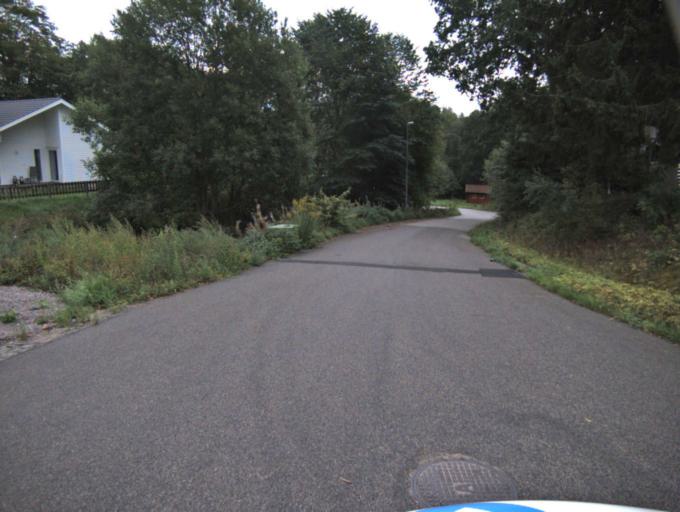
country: SE
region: Vaestra Goetaland
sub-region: Ulricehamns Kommun
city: Ulricehamn
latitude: 57.9243
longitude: 13.4918
